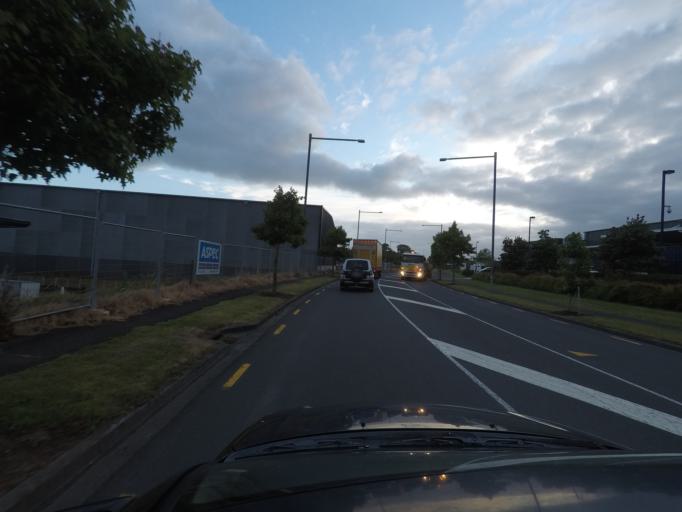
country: NZ
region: Auckland
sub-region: Auckland
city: Tamaki
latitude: -36.9388
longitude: 174.8723
